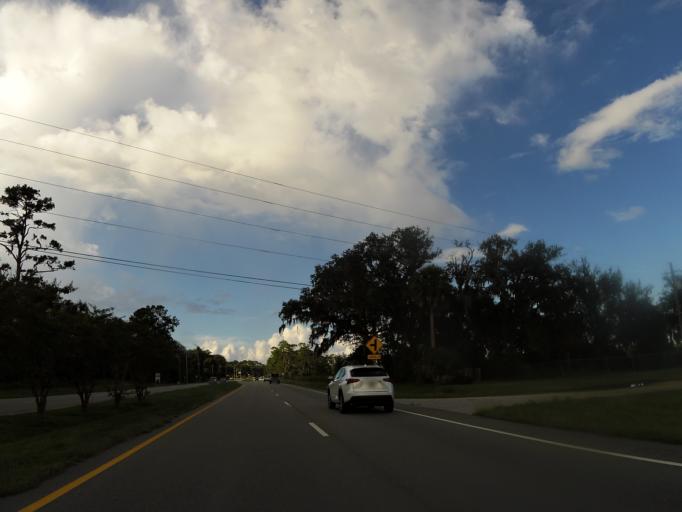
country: US
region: Georgia
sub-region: Glynn County
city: Country Club Estates
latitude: 31.2065
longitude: -81.4670
